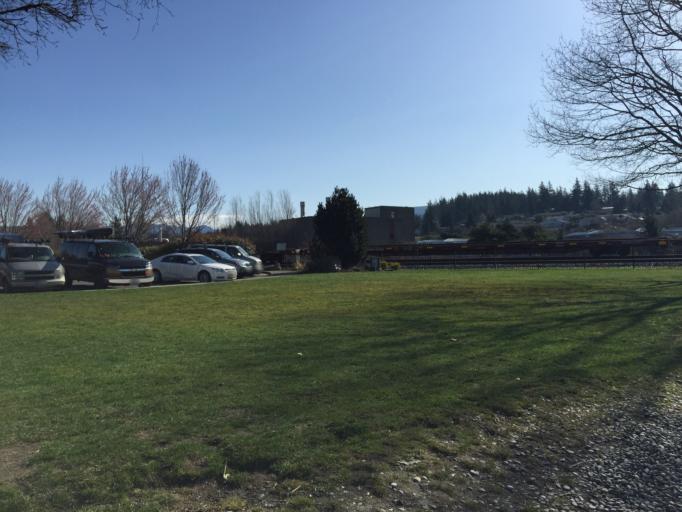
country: US
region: Washington
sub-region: Whatcom County
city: Bellingham
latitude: 48.7192
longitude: -122.5161
